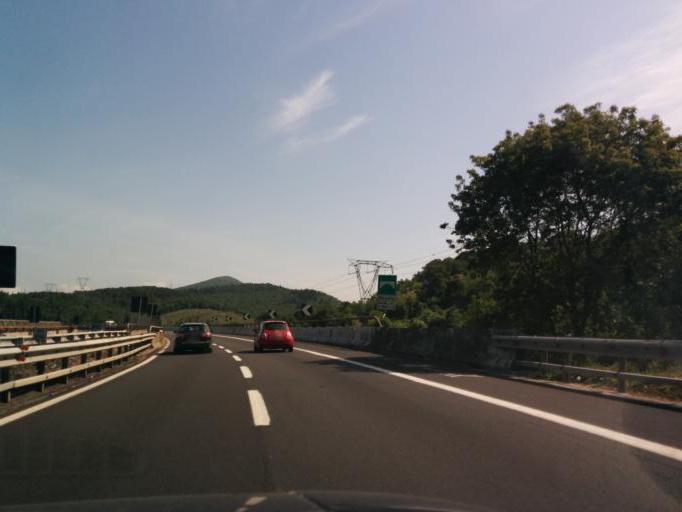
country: IT
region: Tuscany
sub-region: Province of Florence
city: Carraia
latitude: 43.8824
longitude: 11.1841
